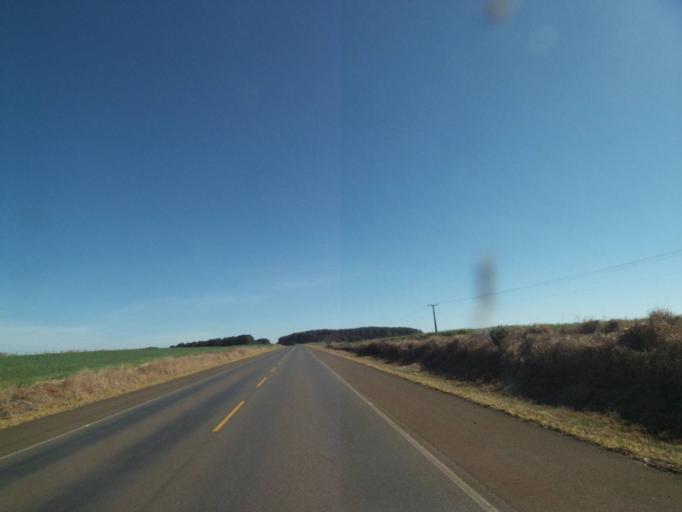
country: BR
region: Parana
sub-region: Tibagi
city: Tibagi
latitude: -24.4306
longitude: -50.4086
